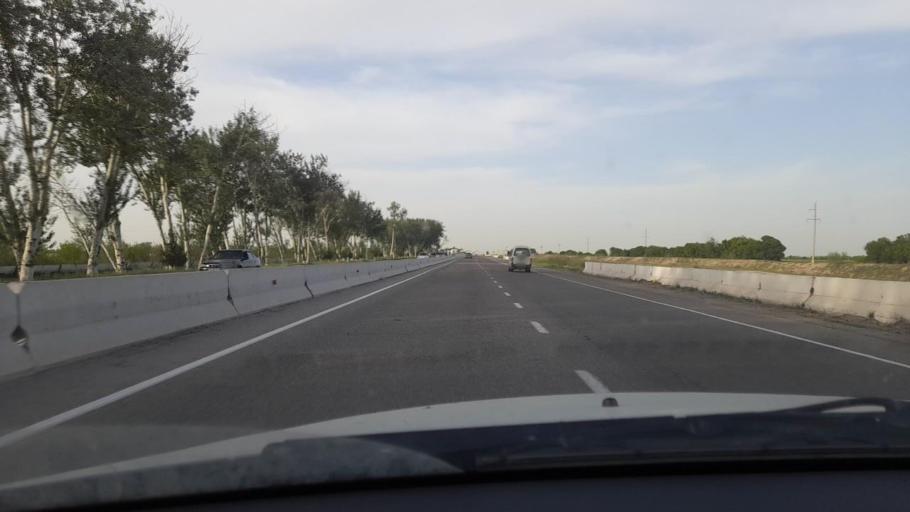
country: UZ
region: Jizzax
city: Dustlik
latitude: 40.4093
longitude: 68.2001
